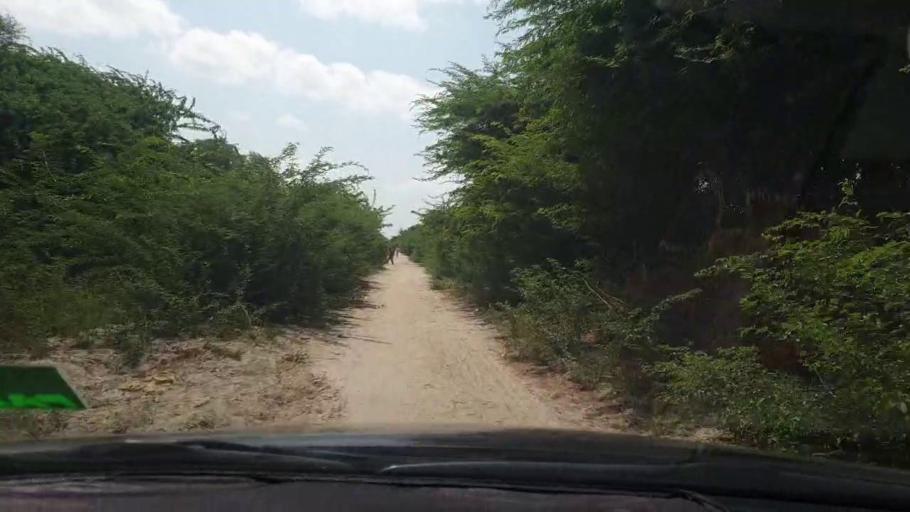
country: PK
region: Sindh
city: Tando Bago
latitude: 24.8690
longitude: 69.0712
